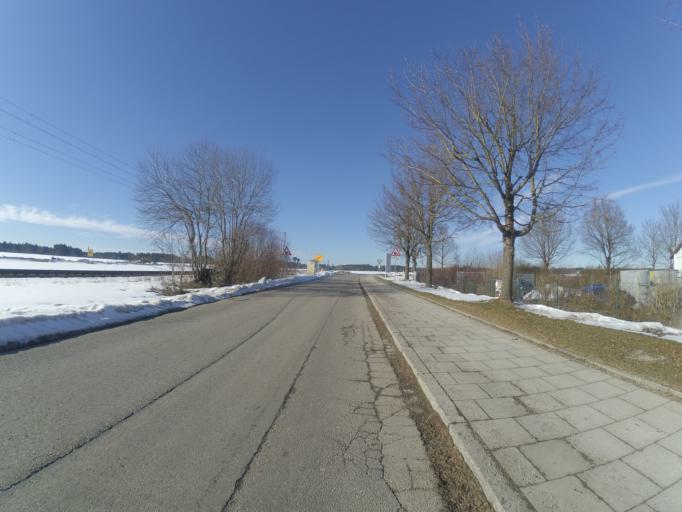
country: DE
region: Bavaria
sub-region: Upper Bavaria
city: Aying
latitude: 47.9715
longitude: 11.7663
